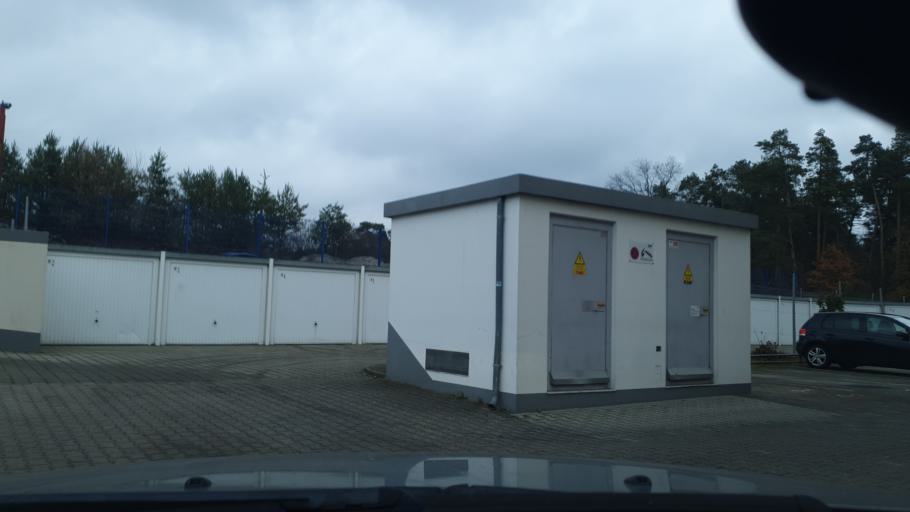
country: DE
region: Rheinland-Pfalz
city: Katzweiler
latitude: 49.4443
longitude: 7.7080
